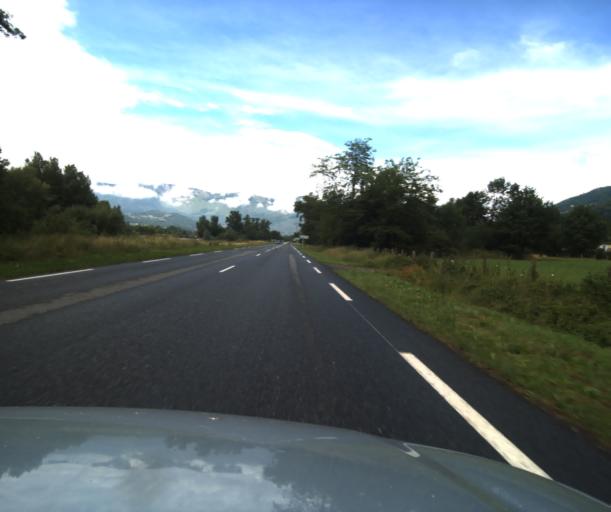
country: FR
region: Midi-Pyrenees
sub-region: Departement des Hautes-Pyrenees
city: Pierrefitte-Nestalas
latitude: 42.9769
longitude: -0.0683
